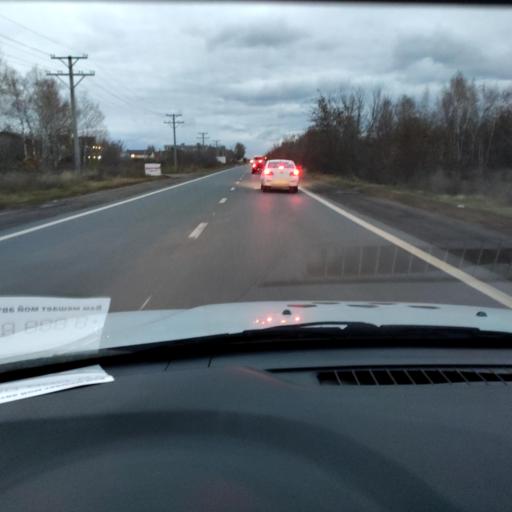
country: RU
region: Samara
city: Tol'yatti
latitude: 53.5557
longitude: 49.3651
